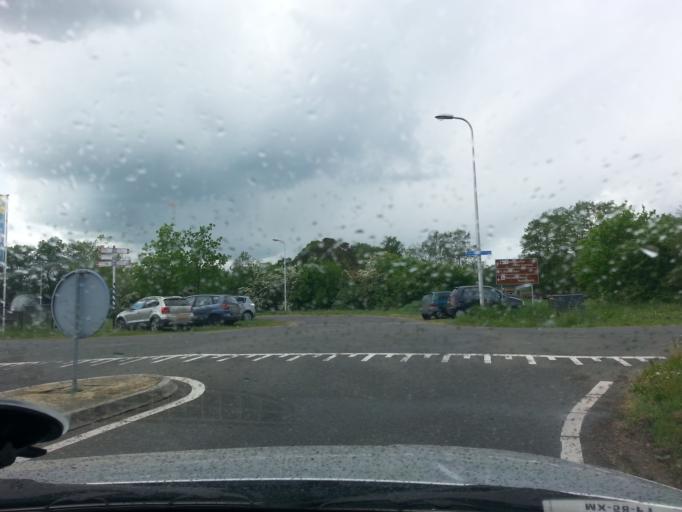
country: NL
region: Overijssel
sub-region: Gemeente Oldenzaal
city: Oldenzaal
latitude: 52.3608
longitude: 6.9880
